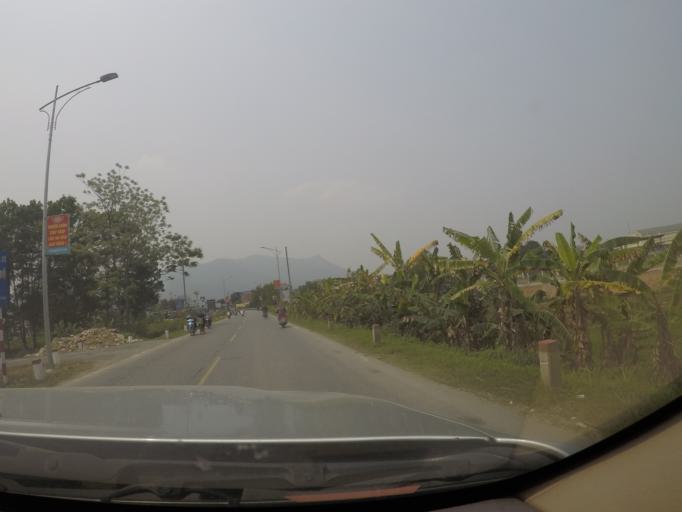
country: VN
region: Thanh Hoa
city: Thi Tran Cam Thuy
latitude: 20.2118
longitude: 105.4792
